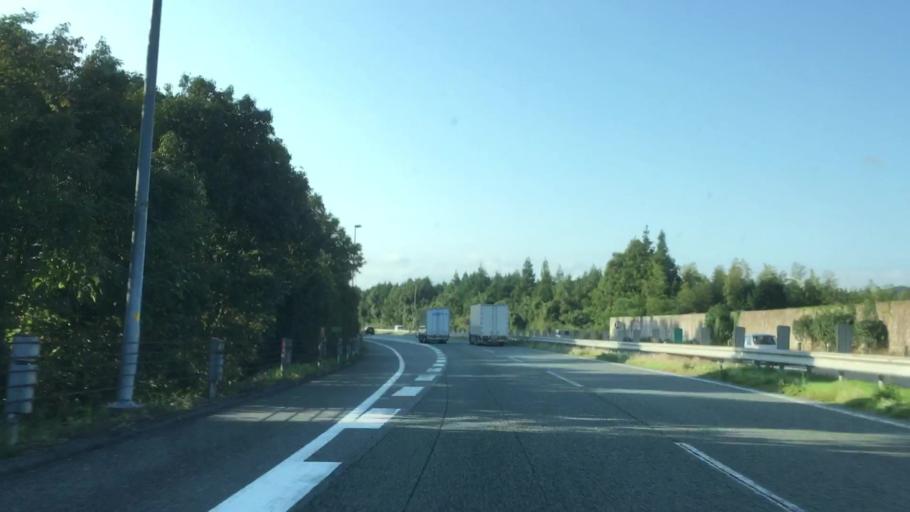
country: JP
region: Yamaguchi
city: Ogori-shimogo
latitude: 34.1508
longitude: 131.3418
